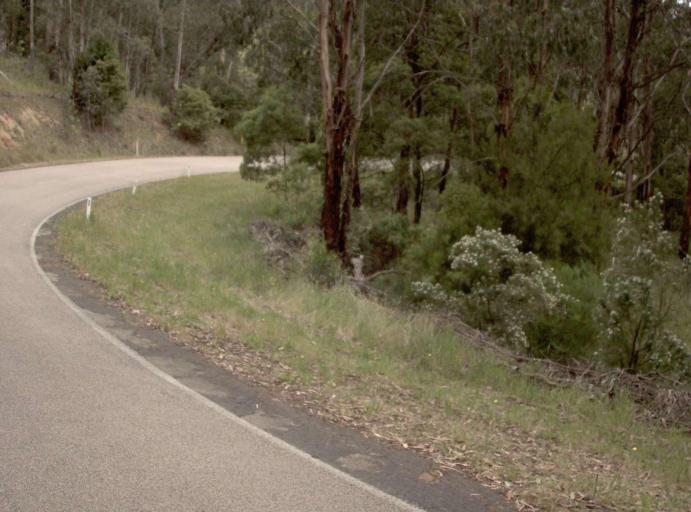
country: AU
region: Victoria
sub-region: East Gippsland
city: Bairnsdale
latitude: -37.5889
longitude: 147.1835
